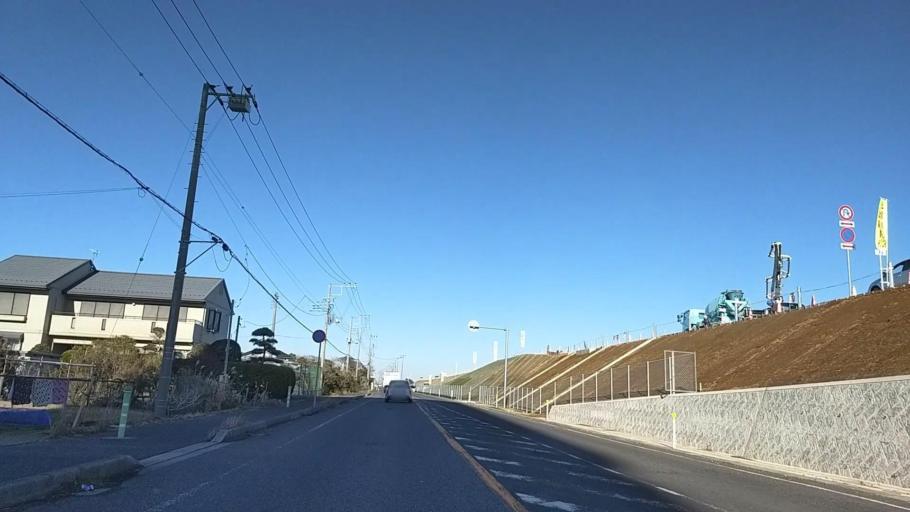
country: JP
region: Chiba
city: Togane
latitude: 35.4537
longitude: 140.4043
